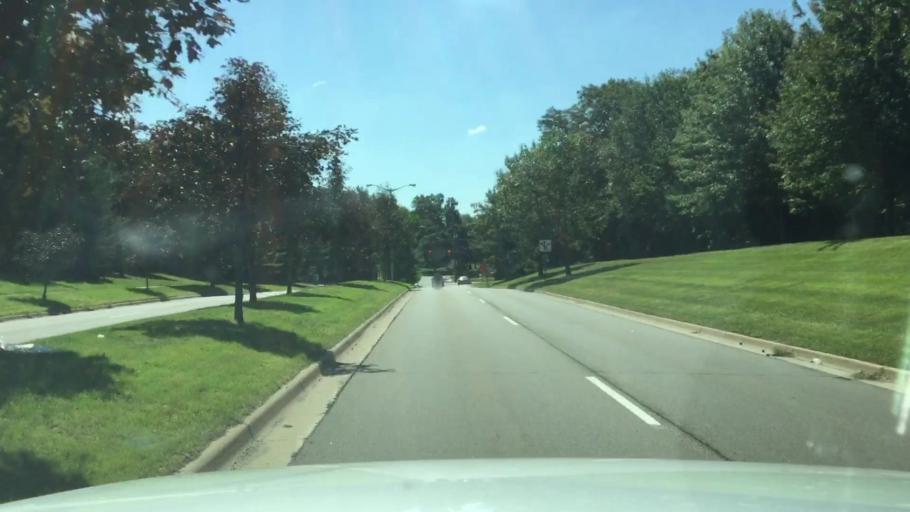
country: US
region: Michigan
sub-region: Kalamazoo County
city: Portage
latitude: 42.2172
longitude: -85.6032
